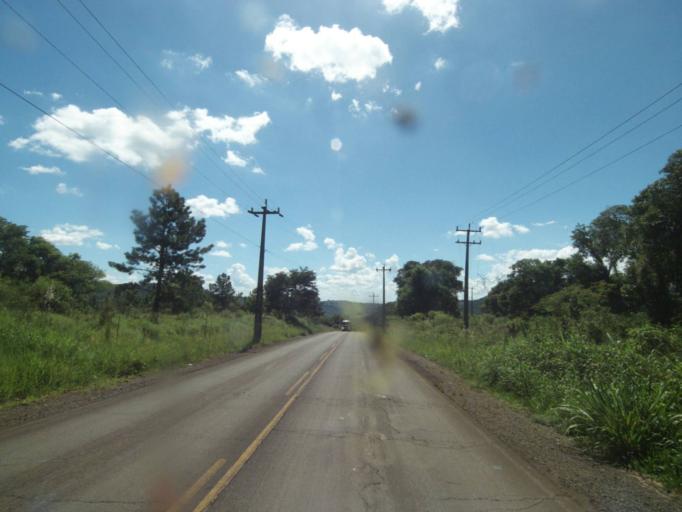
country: BR
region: Parana
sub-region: Chopinzinho
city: Chopinzinho
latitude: -25.7782
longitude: -52.1082
